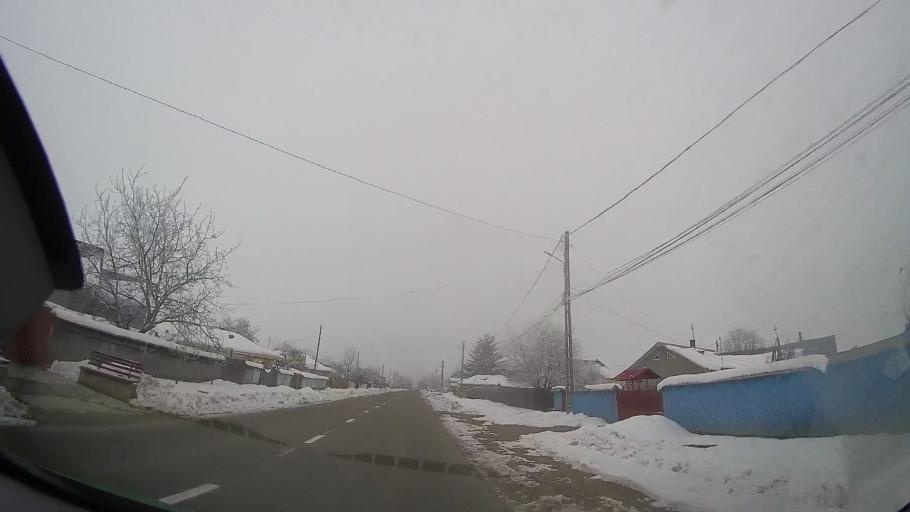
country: RO
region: Neamt
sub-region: Comuna Horia
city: Cotu Vames
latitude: 46.8973
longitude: 26.9587
